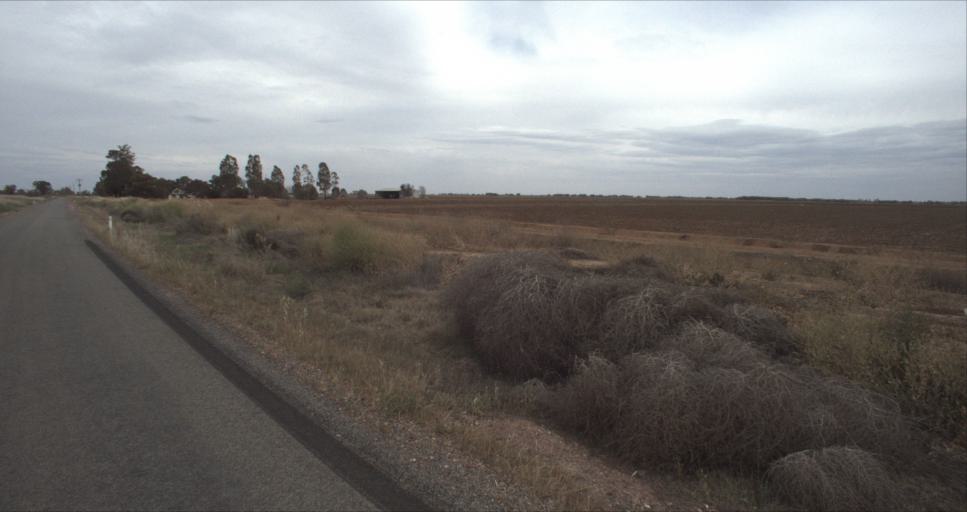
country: AU
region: New South Wales
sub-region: Leeton
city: Leeton
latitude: -34.4294
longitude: 146.3778
